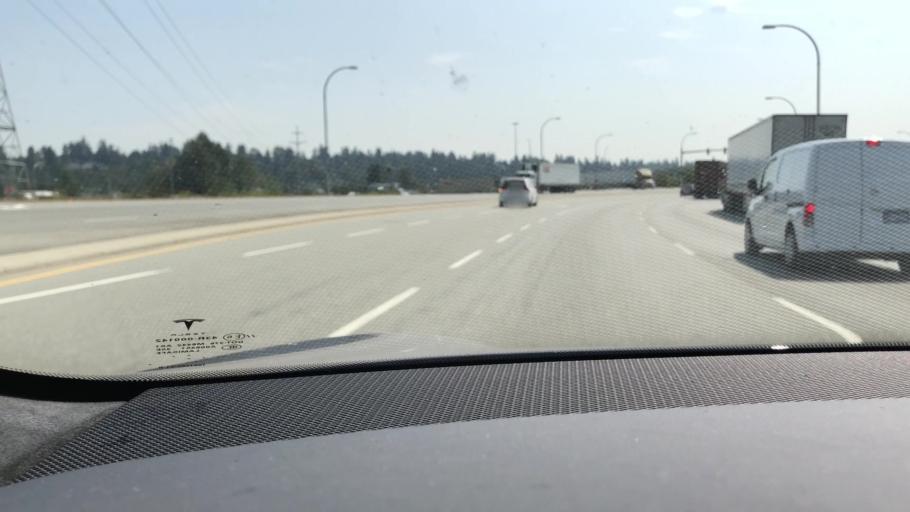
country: CA
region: British Columbia
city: Delta
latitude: 49.1462
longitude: -122.9462
